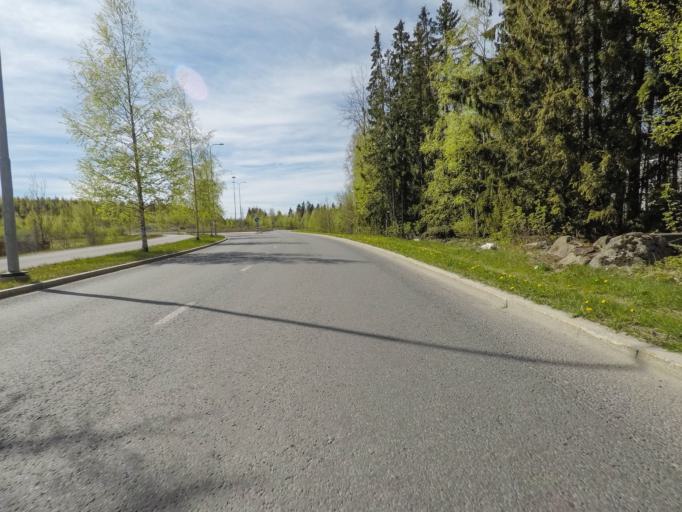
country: FI
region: Pirkanmaa
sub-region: Tampere
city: Tampere
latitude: 61.4534
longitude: 23.7626
